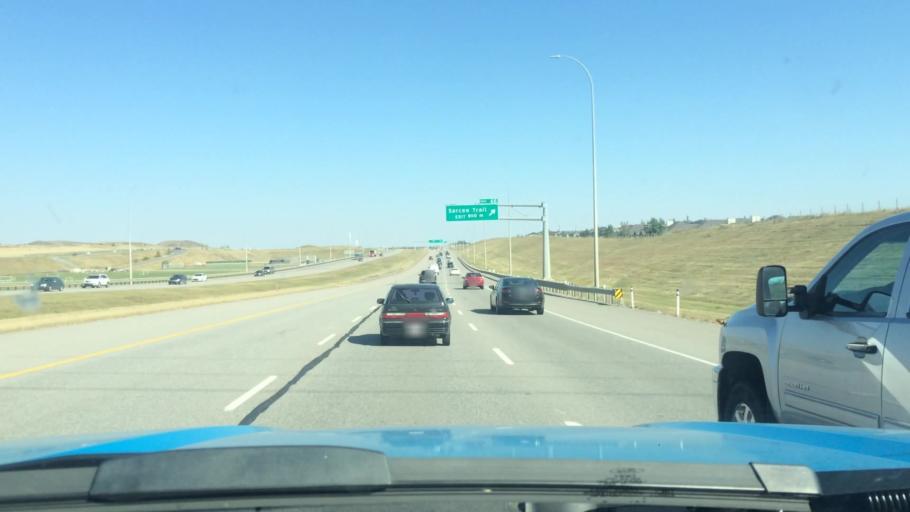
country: CA
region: Alberta
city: Calgary
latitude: 51.1506
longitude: -114.1882
